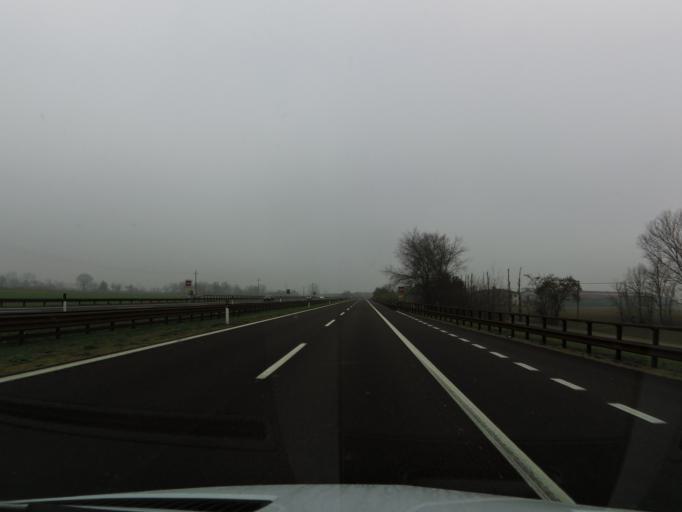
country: IT
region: Lombardy
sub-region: Provincia di Mantova
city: Bondeno
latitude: 44.9627
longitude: 10.8601
